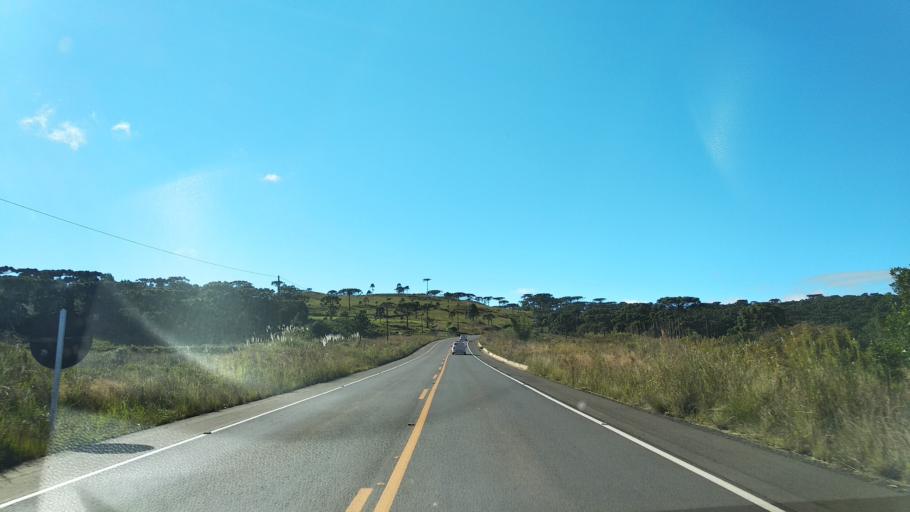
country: BR
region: Santa Catarina
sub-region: Lages
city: Lages
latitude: -27.8941
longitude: -50.1339
